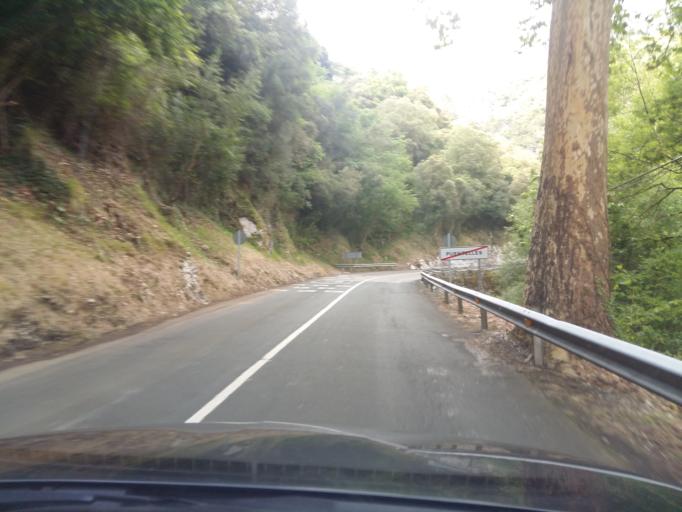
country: ES
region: Cantabria
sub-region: Provincia de Cantabria
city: Tresviso
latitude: 43.3153
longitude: -4.6070
